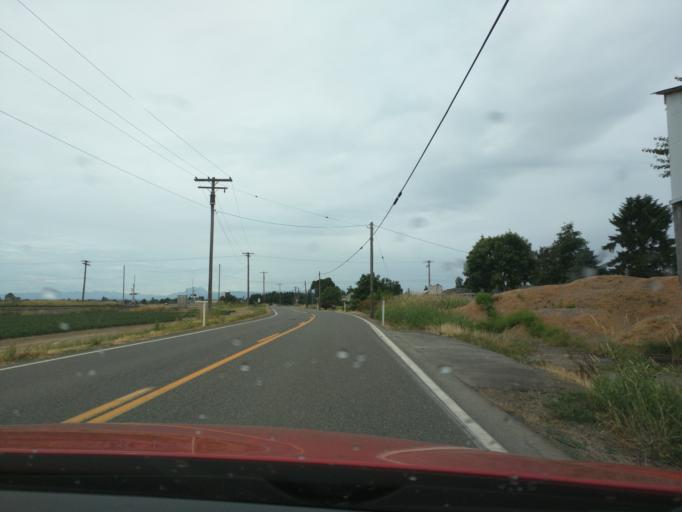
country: US
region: Washington
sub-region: Whatcom County
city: Nooksack
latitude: 48.9043
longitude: -122.3205
